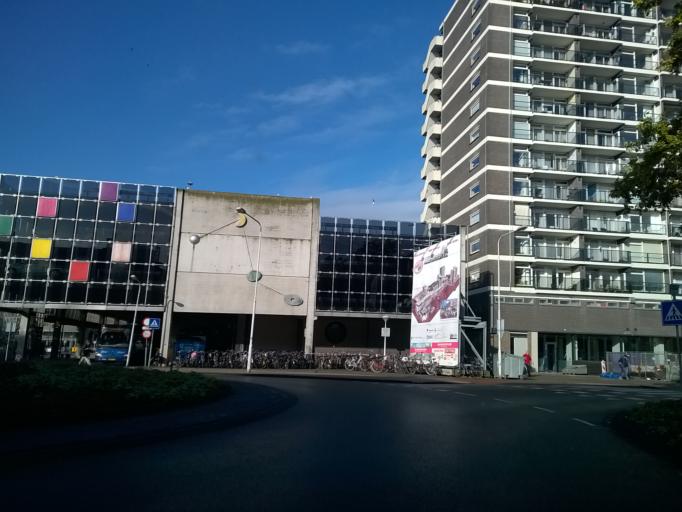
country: NL
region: Friesland
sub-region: Gemeente Smallingerland
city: Drachten
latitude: 53.1037
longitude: 6.1015
